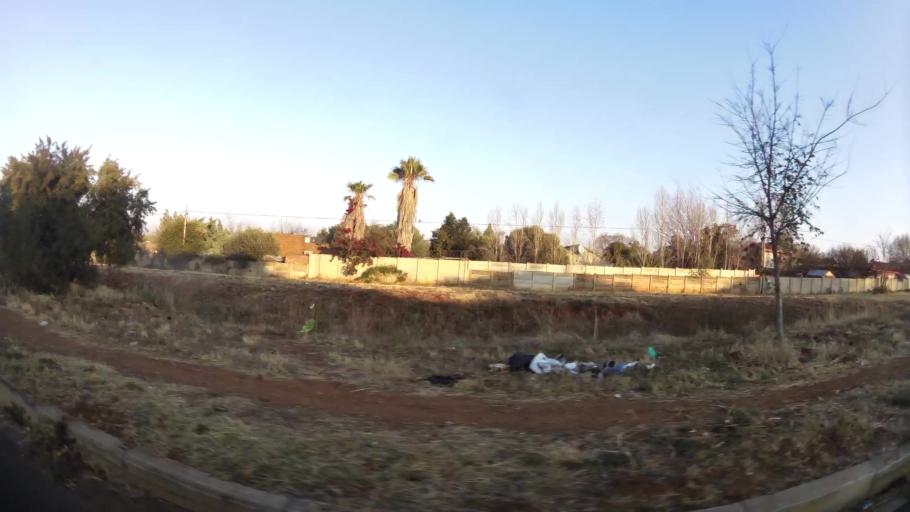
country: ZA
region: Orange Free State
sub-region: Mangaung Metropolitan Municipality
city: Bloemfontein
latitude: -29.0978
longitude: 26.1638
